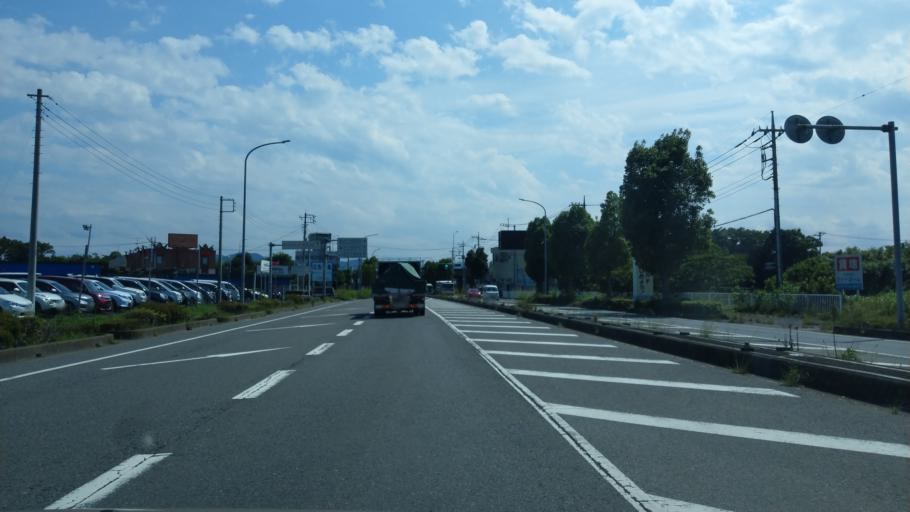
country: JP
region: Saitama
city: Honjo
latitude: 36.2224
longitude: 139.1643
